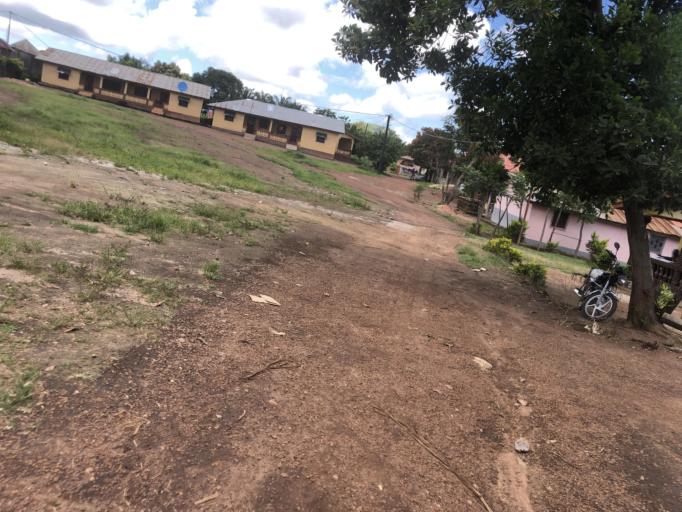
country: SL
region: Northern Province
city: Makeni
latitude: 8.8606
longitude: -12.0443
